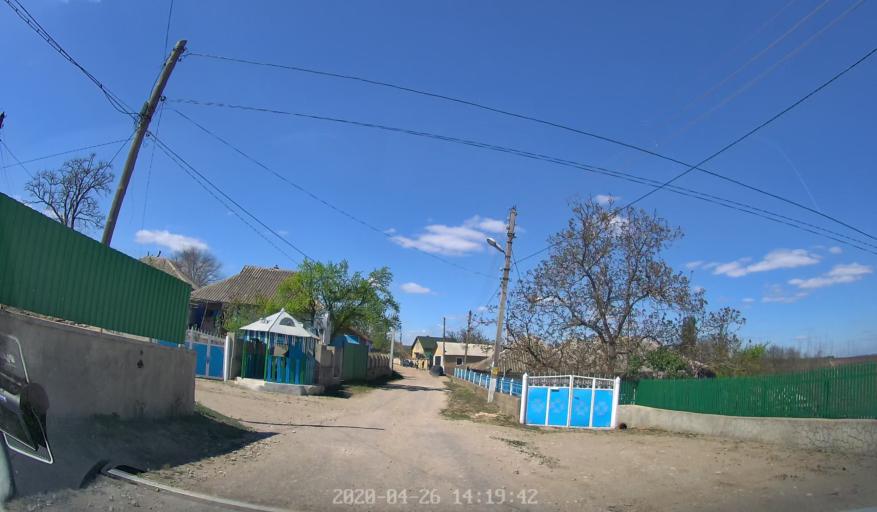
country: MD
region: Telenesti
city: Cocieri
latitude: 47.3562
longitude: 29.0596
